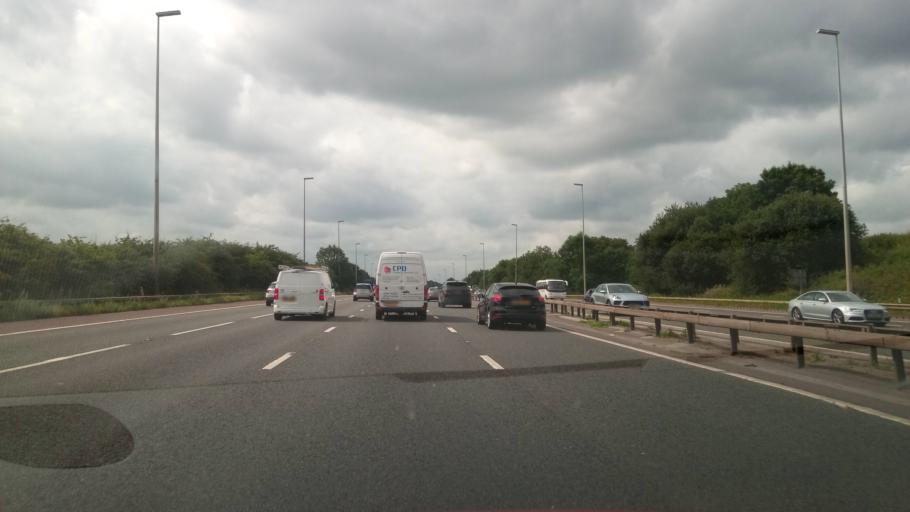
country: GB
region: England
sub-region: Lancashire
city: Clayton-le-Woods
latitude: 53.7532
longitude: -2.6410
